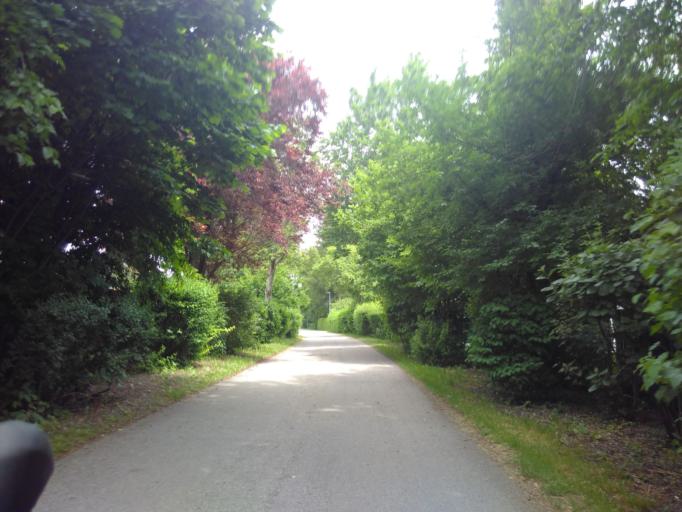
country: DE
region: Bavaria
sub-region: Upper Bavaria
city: Eichenau
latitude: 48.1556
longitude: 11.3216
